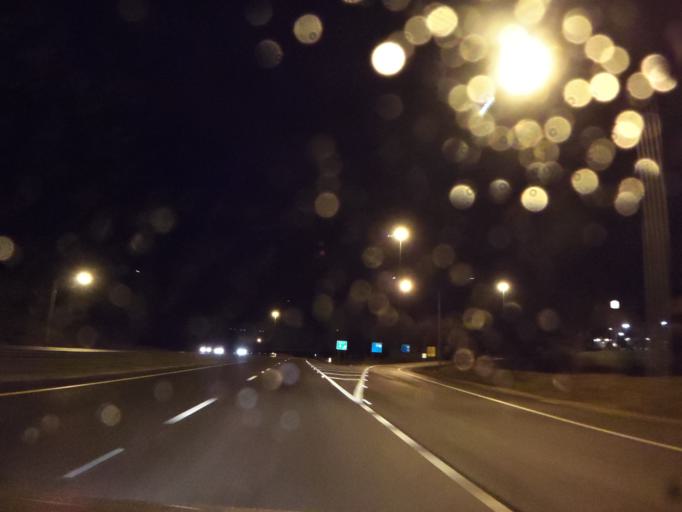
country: US
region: Tennessee
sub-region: Jefferson County
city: White Pine
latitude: 36.1378
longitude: -83.2756
